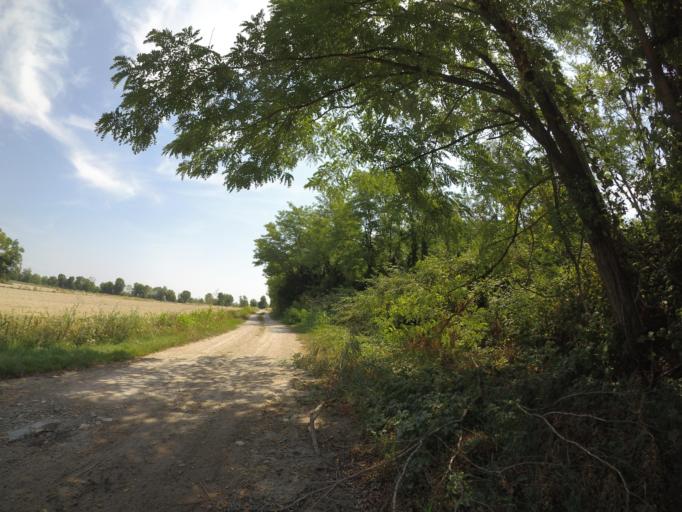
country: IT
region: Friuli Venezia Giulia
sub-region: Provincia di Pordenone
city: Rosa
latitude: 45.9400
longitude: 12.8956
